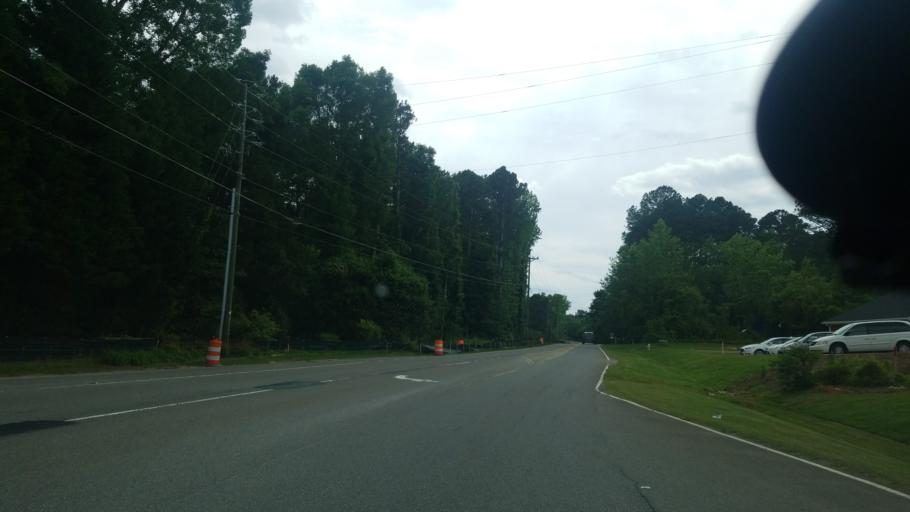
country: US
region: Georgia
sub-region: Forsyth County
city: Cumming
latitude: 34.1828
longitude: -84.1243
